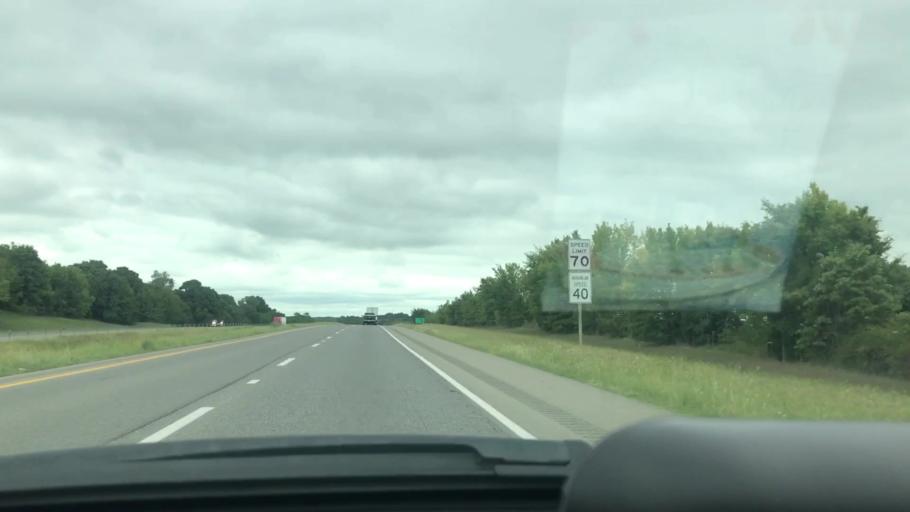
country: US
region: Oklahoma
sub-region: McIntosh County
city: Eufaula
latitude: 35.3717
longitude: -95.5710
